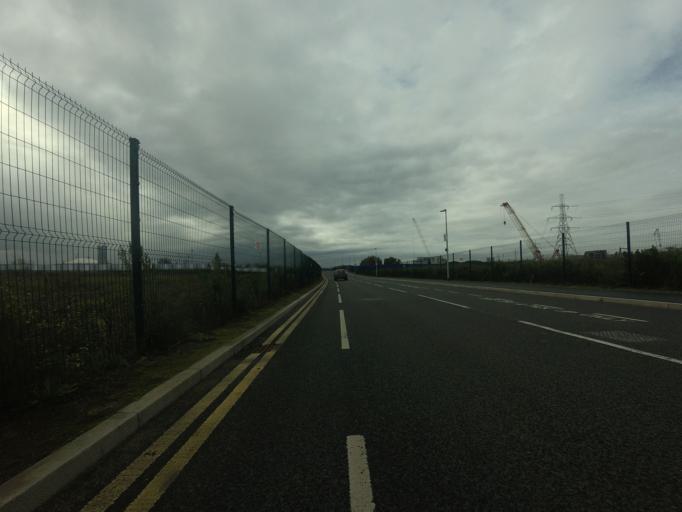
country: GB
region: England
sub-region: Greater London
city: Becontree
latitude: 51.5199
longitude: 0.1189
